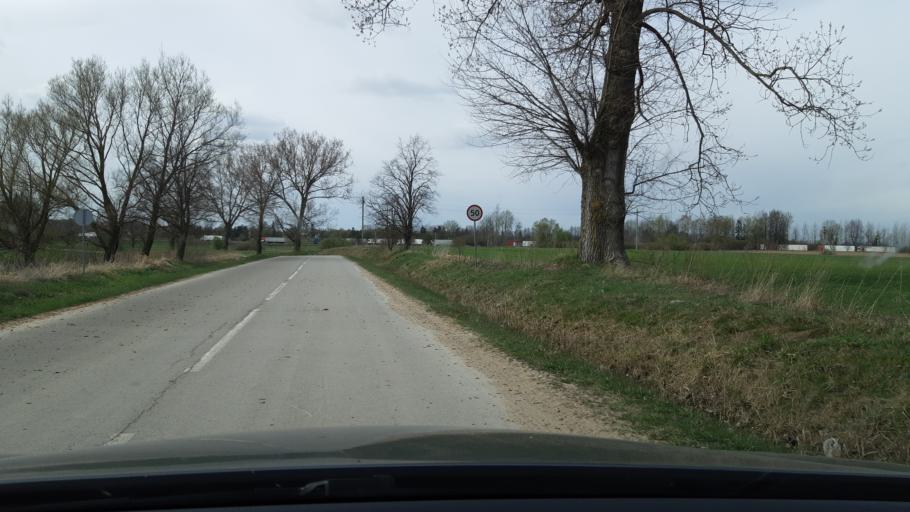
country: LT
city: Virbalis
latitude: 54.6215
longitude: 22.8370
